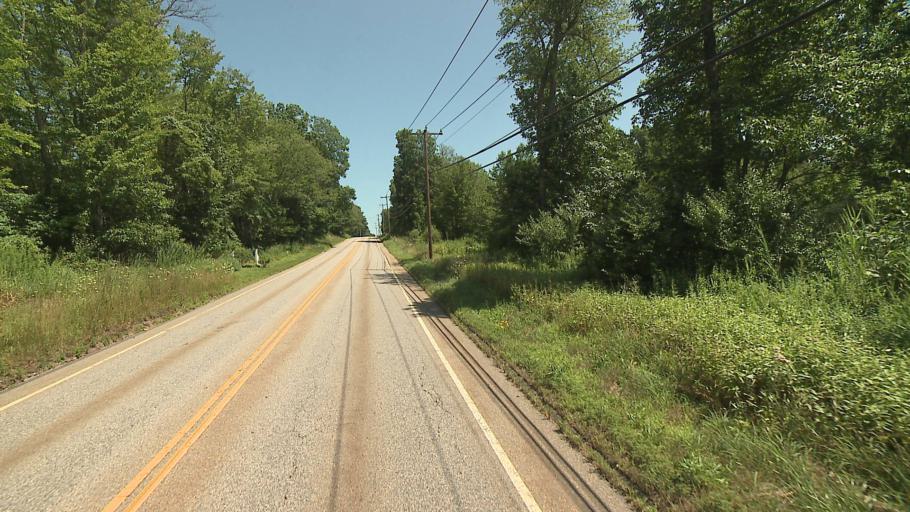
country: US
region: Connecticut
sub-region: Litchfield County
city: Northwest Harwinton
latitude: 41.7767
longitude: -73.0191
